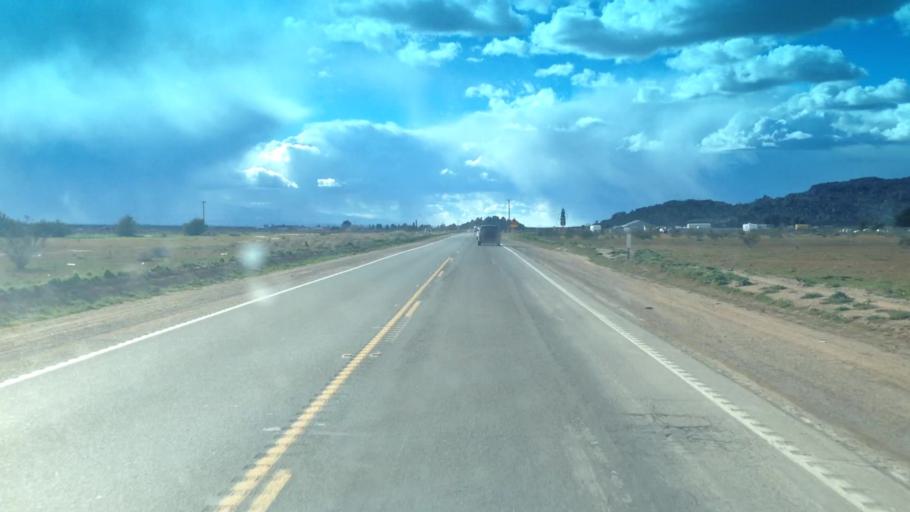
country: US
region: California
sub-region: San Bernardino County
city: Apple Valley
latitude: 34.4719
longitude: -117.0993
